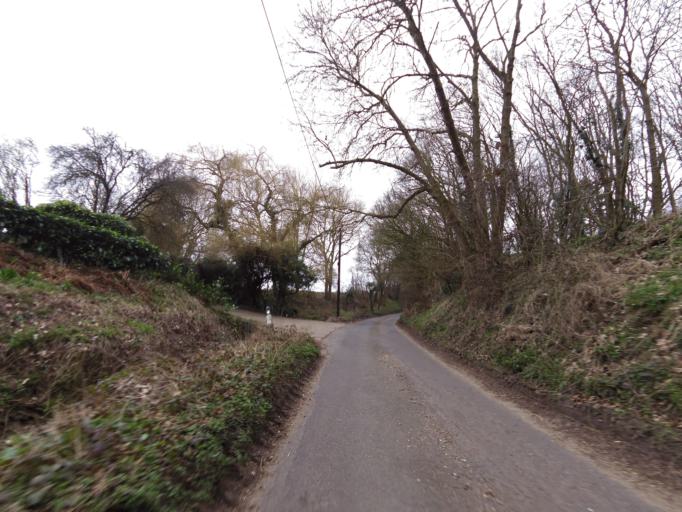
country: GB
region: England
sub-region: Suffolk
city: Cookley
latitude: 52.2657
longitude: 1.4432
